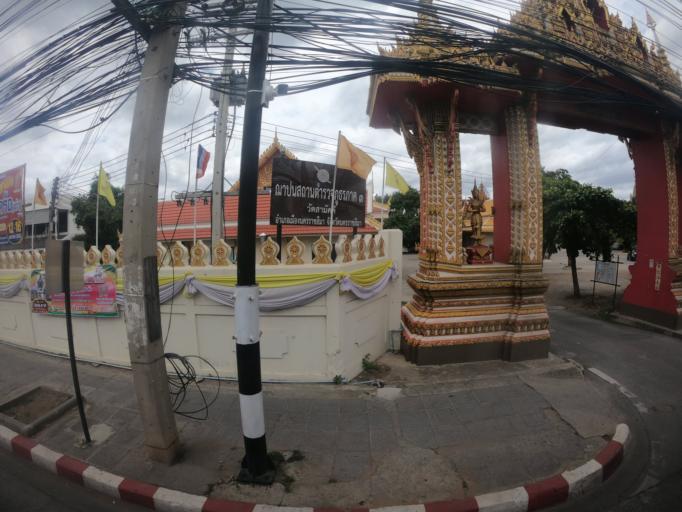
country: TH
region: Nakhon Ratchasima
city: Nakhon Ratchasima
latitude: 14.9802
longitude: 102.1055
